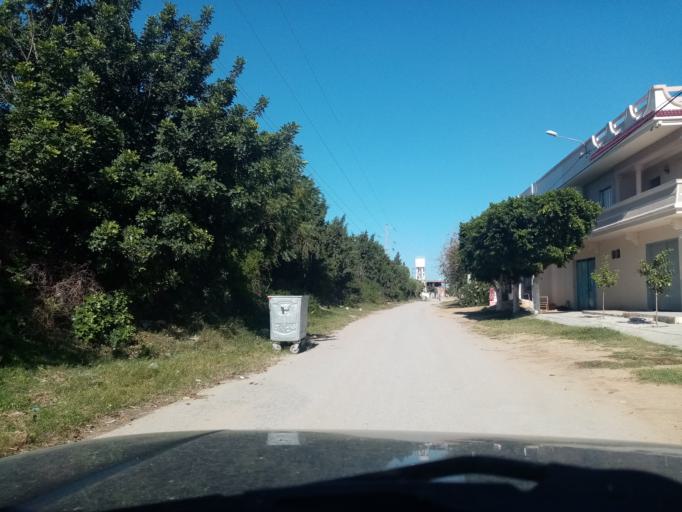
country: TN
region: Nabul
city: Bu `Urqub
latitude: 36.5730
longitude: 10.5740
